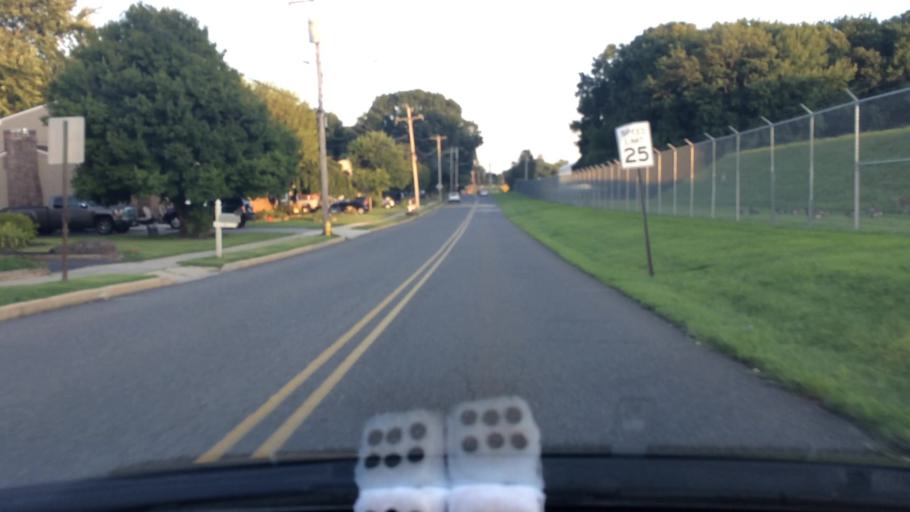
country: US
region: Pennsylvania
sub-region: Delaware County
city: Village Green-Green Ridge
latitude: 39.8645
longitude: -75.4512
